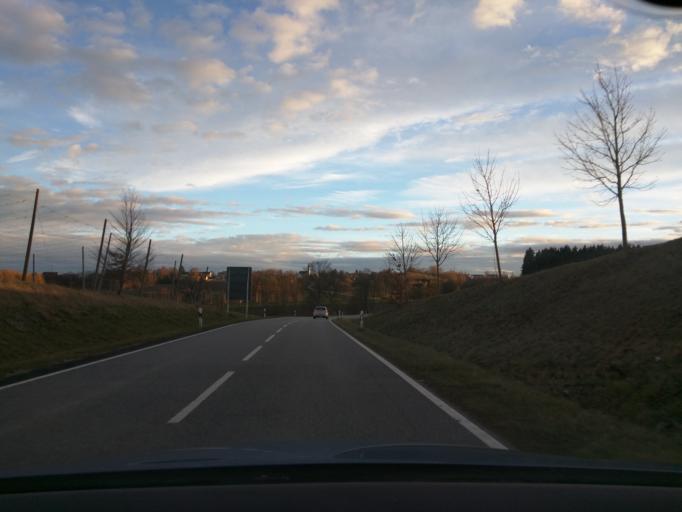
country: DE
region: Bavaria
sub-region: Upper Bavaria
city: Attenkirchen
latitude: 48.5175
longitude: 11.7548
